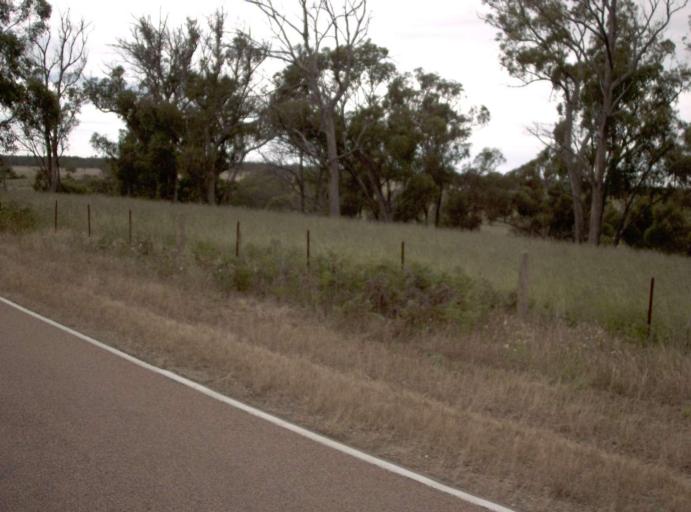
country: AU
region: Victoria
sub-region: Wellington
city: Sale
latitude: -38.0052
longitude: 147.2856
